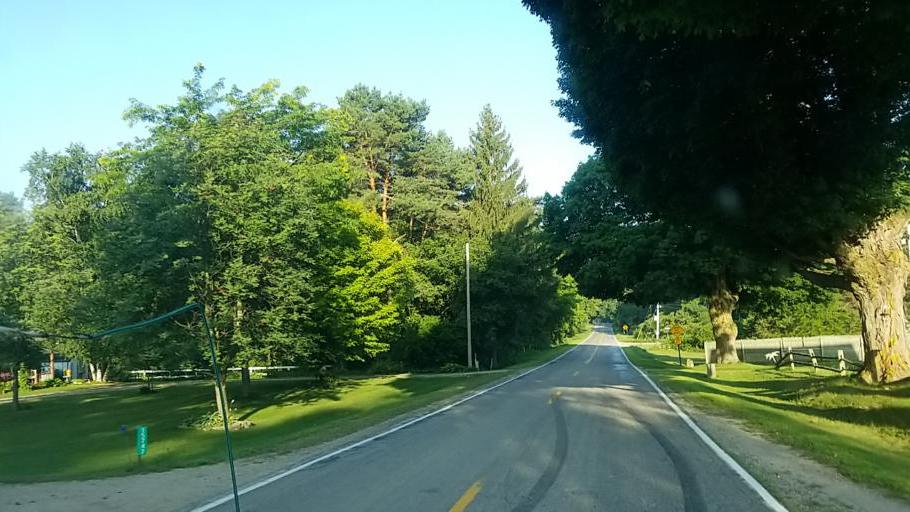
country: US
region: Michigan
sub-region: Montcalm County
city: Howard City
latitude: 43.3595
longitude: -85.3978
